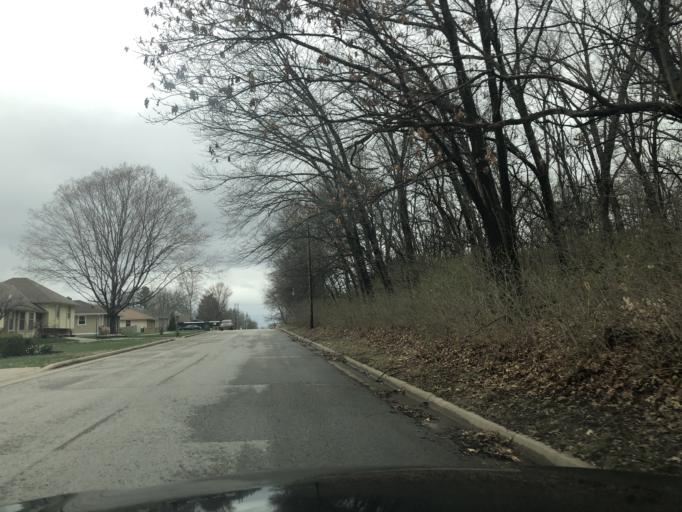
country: US
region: Kansas
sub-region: Leavenworth County
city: Leavenworth
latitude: 39.2796
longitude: -94.9138
